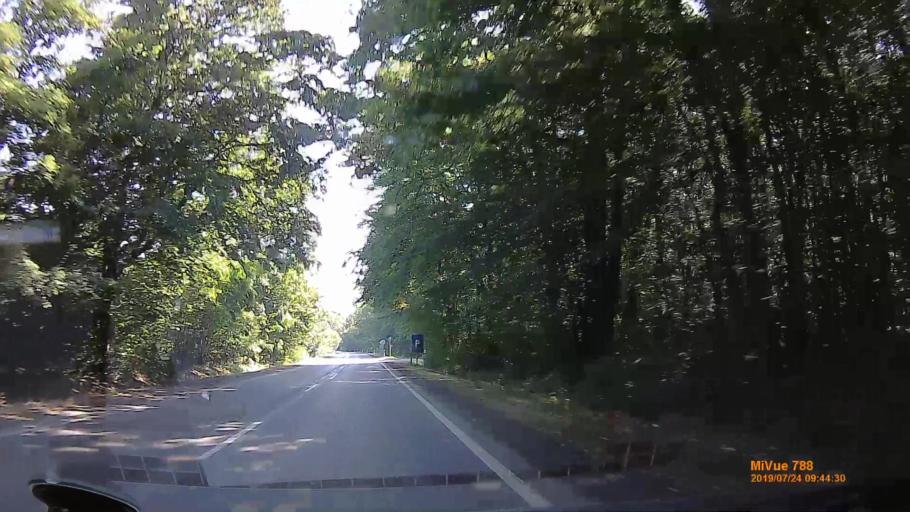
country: HU
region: Szabolcs-Szatmar-Bereg
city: Baktaloranthaza
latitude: 47.9807
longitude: 22.0512
